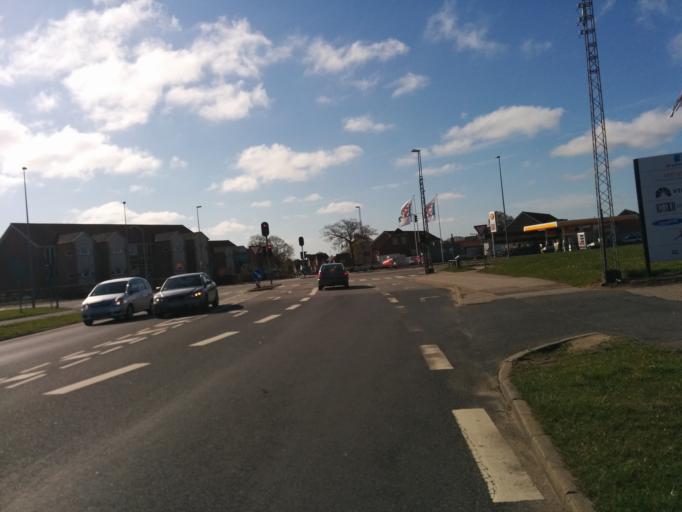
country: DK
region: Central Jutland
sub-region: Viborg Kommune
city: Viborg
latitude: 56.4633
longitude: 9.4039
